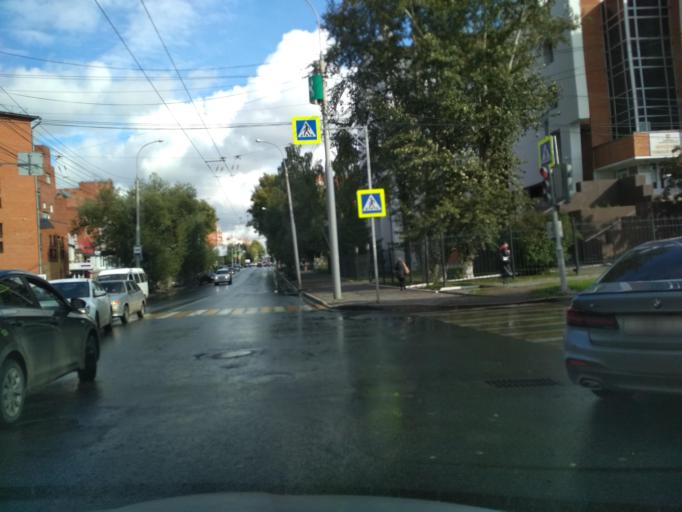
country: RU
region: Tomsk
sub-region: Tomskiy Rayon
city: Tomsk
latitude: 56.4762
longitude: 84.9580
